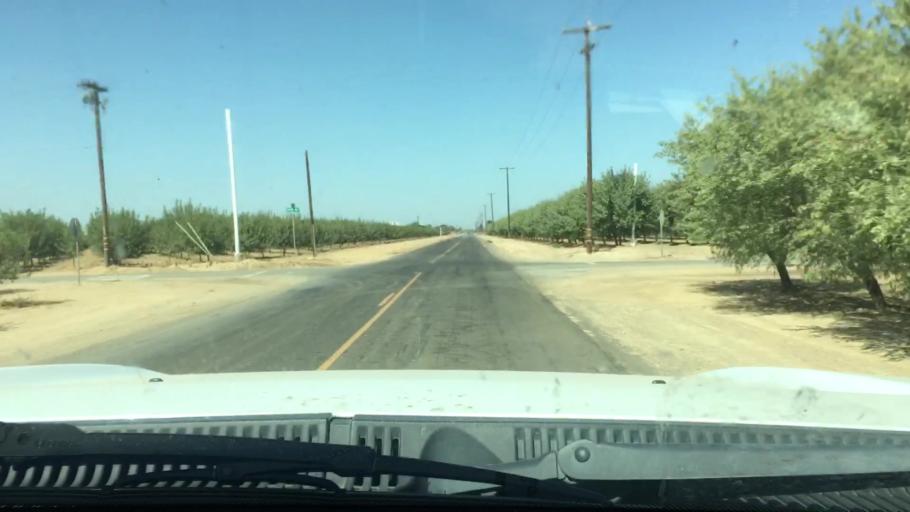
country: US
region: California
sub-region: Kern County
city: Shafter
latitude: 35.4634
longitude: -119.3143
